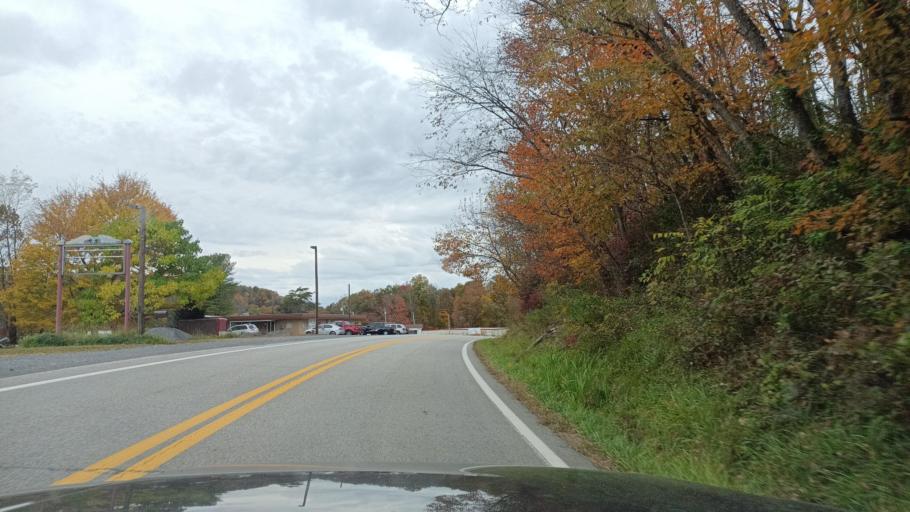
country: US
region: West Virginia
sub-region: Taylor County
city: Grafton
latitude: 39.3413
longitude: -79.9894
